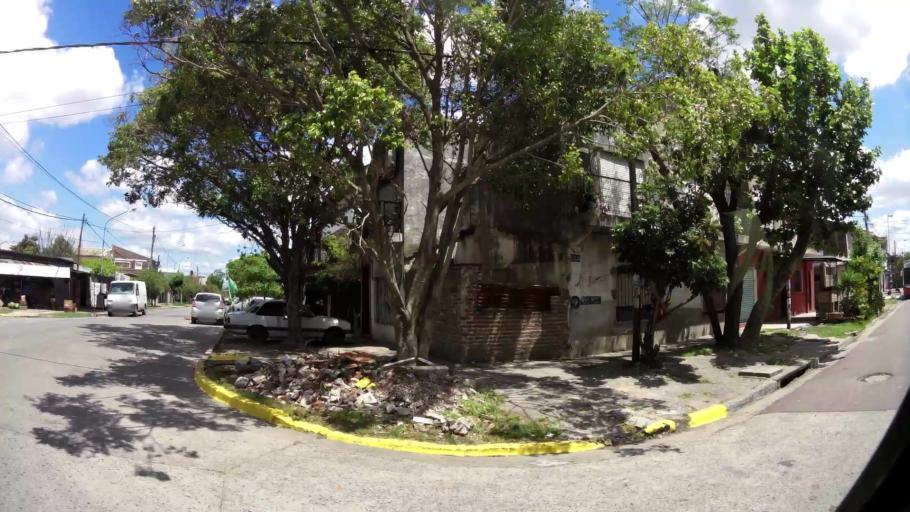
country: AR
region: Buenos Aires
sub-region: Partido de Lanus
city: Lanus
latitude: -34.6995
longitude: -58.4334
